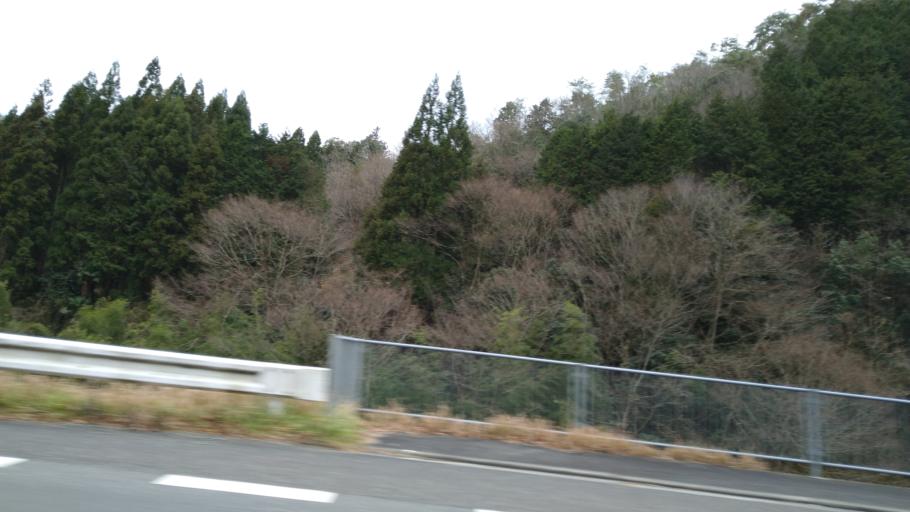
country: JP
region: Kyoto
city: Ayabe
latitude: 35.2575
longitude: 135.2764
